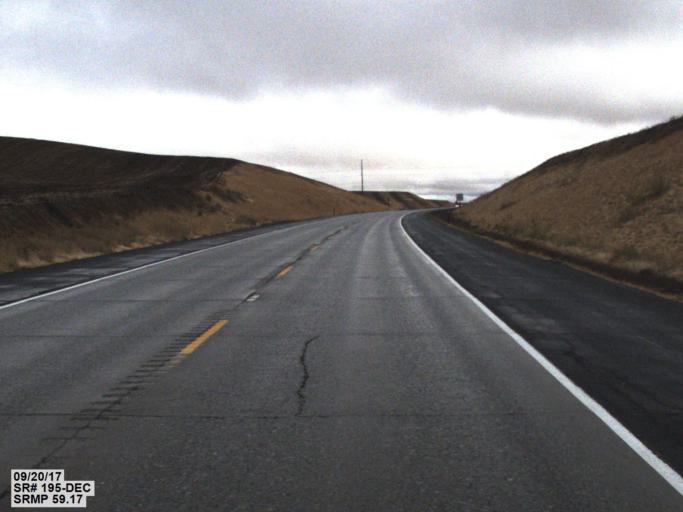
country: US
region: Washington
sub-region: Whitman County
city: Colfax
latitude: 47.1628
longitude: -117.3785
